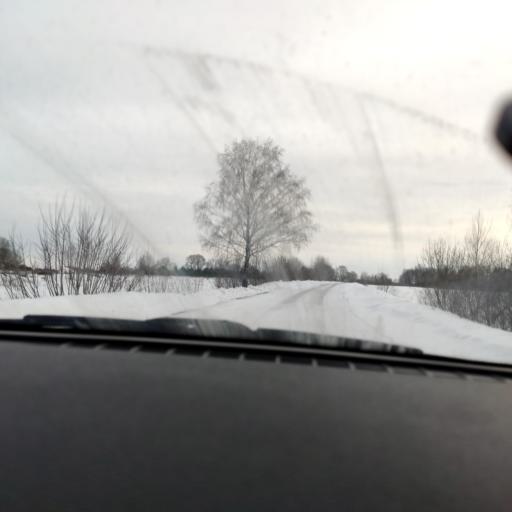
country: RU
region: Bashkortostan
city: Iglino
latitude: 54.7660
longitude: 56.5338
